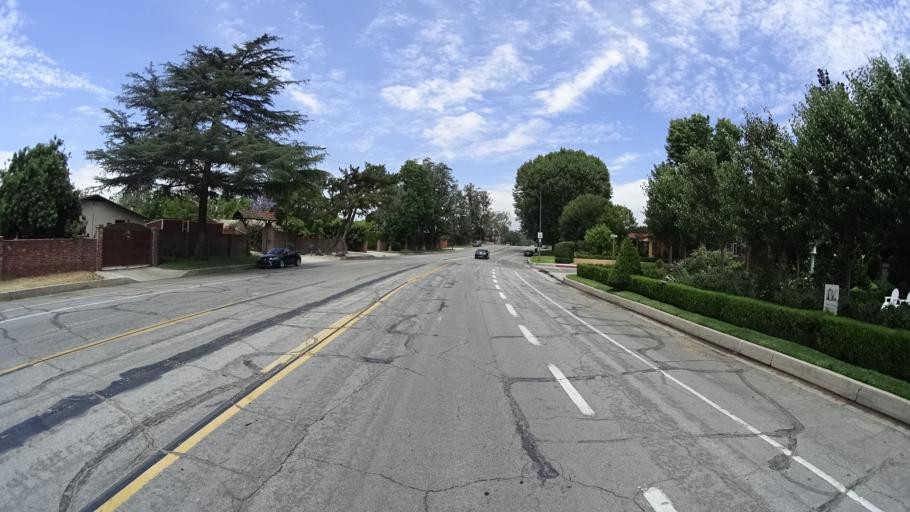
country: US
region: California
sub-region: Los Angeles County
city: Burbank
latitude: 34.1598
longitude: -118.3035
